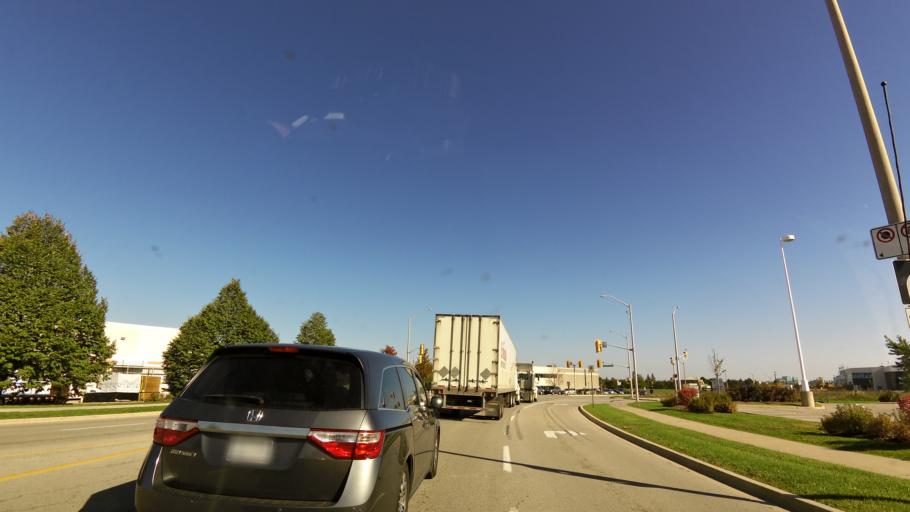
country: CA
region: Ontario
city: Oakville
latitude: 43.5171
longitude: -79.6853
